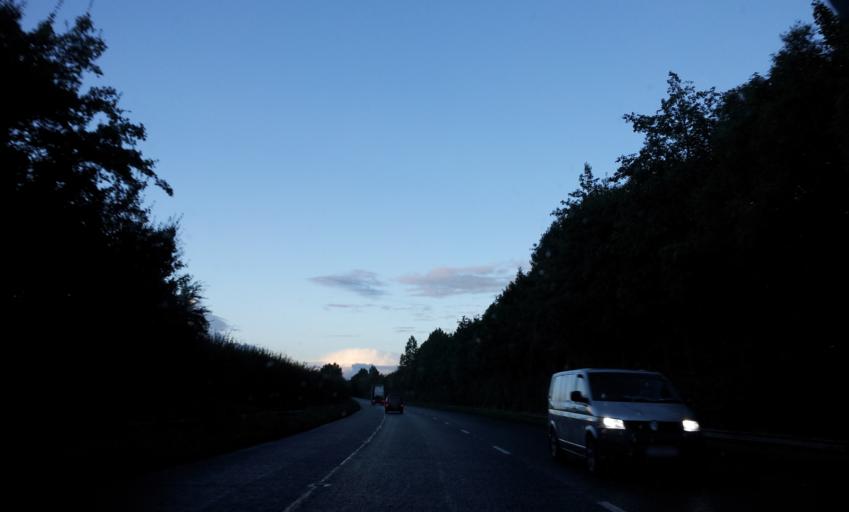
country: IE
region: Munster
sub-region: County Limerick
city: Rathkeale
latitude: 52.5202
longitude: -8.9500
